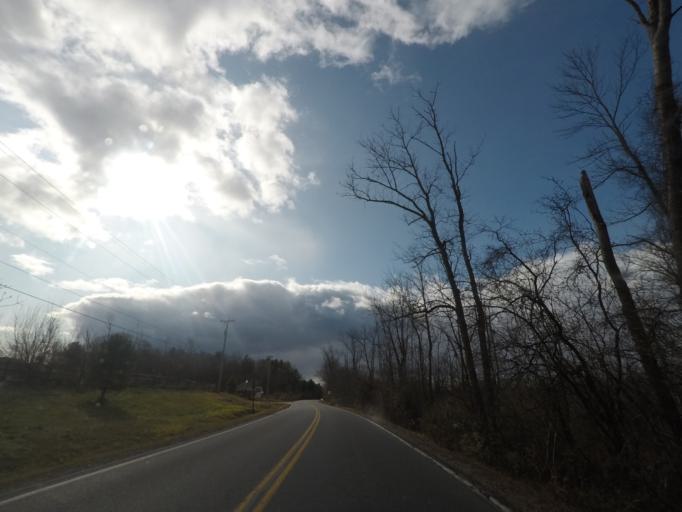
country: US
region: New York
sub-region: Saratoga County
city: Ballston Spa
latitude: 42.9603
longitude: -73.8424
